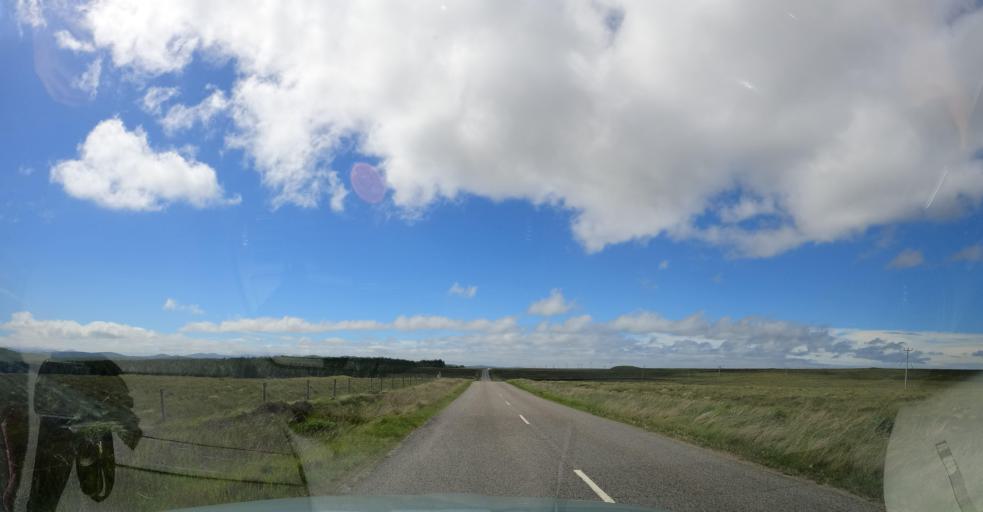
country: GB
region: Scotland
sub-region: Eilean Siar
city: Isle of Lewis
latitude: 58.1784
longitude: -6.6377
